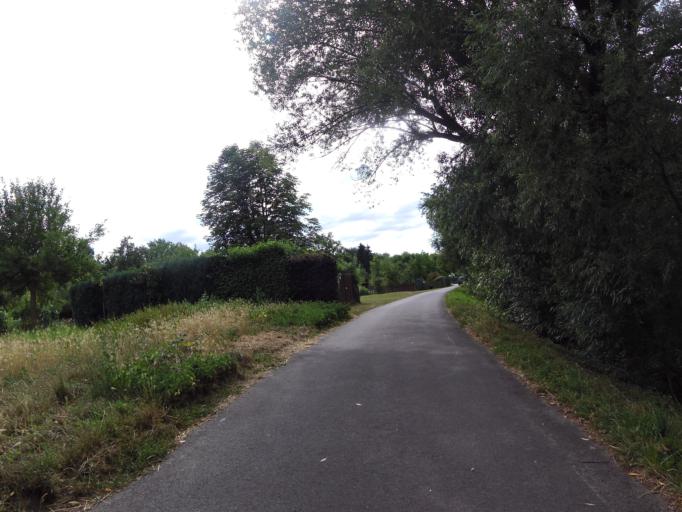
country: DE
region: Bavaria
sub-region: Regierungsbezirk Unterfranken
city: Randersacker
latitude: 49.7630
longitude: 9.9620
